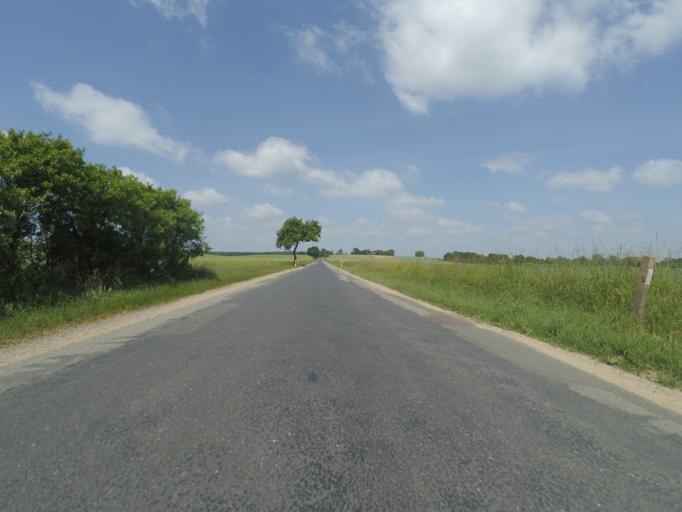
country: DE
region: Mecklenburg-Vorpommern
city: Lubz
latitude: 53.4104
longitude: 12.0134
